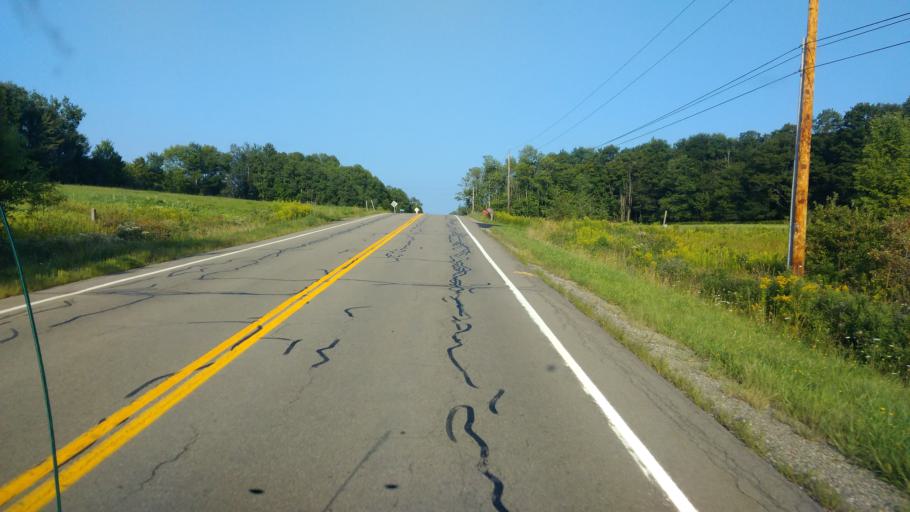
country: US
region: New York
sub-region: Allegany County
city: Andover
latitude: 42.1542
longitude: -77.7014
